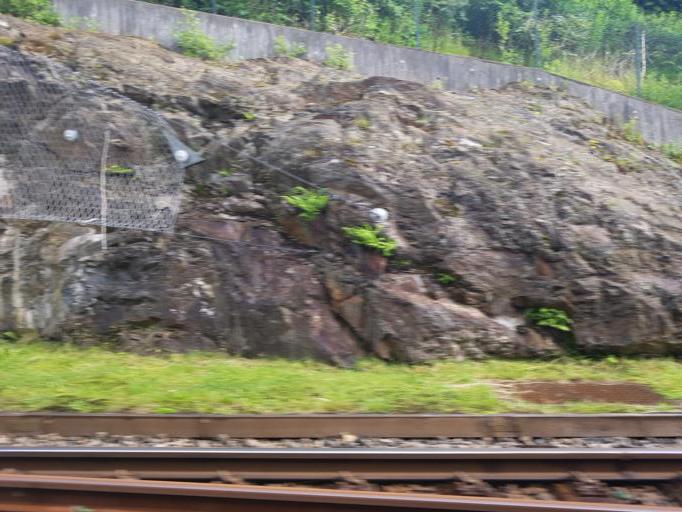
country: NO
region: Hordaland
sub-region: Bergen
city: Sandsli
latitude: 60.3092
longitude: 5.3468
